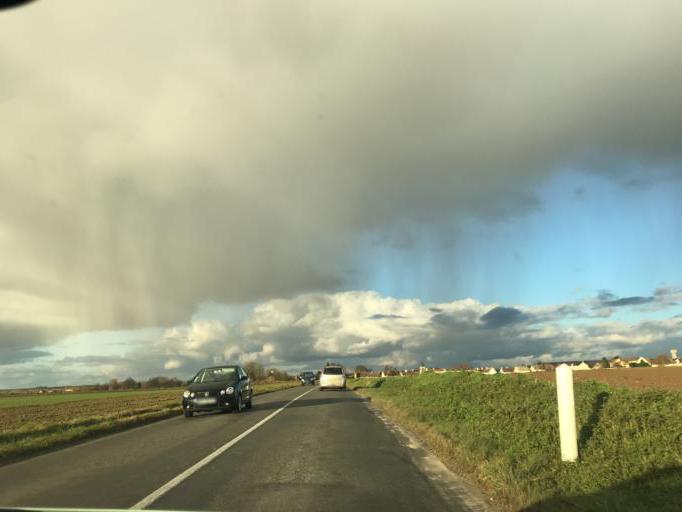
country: FR
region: Ile-de-France
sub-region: Departement de Seine-et-Marne
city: Claye-Souilly
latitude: 48.9604
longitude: 2.6985
